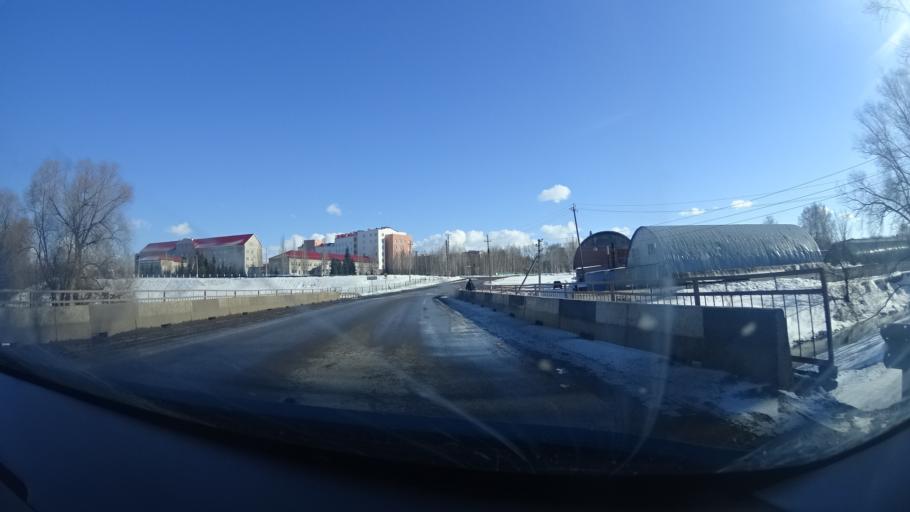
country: RU
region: Bashkortostan
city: Chishmy
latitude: 54.5918
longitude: 55.3672
